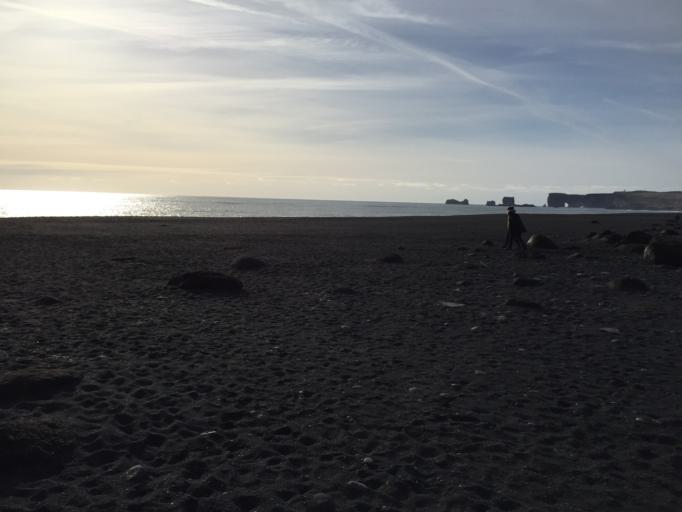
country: IS
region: South
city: Vestmannaeyjar
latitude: 63.4037
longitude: -19.0446
